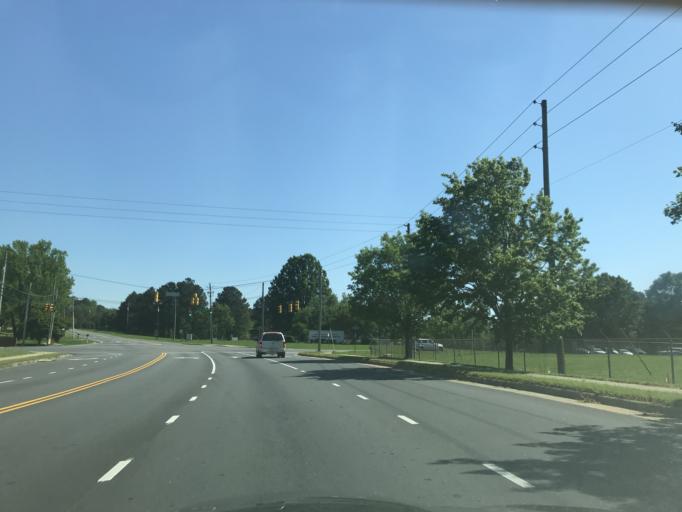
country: US
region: North Carolina
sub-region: Wake County
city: Garner
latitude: 35.7320
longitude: -78.6278
